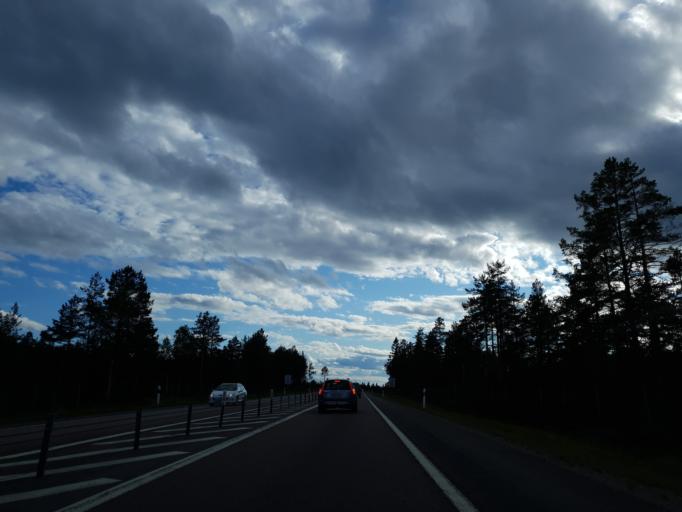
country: SE
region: Vaesternorrland
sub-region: Haernoesands Kommun
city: Haernoesand
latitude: 62.5674
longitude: 17.7358
